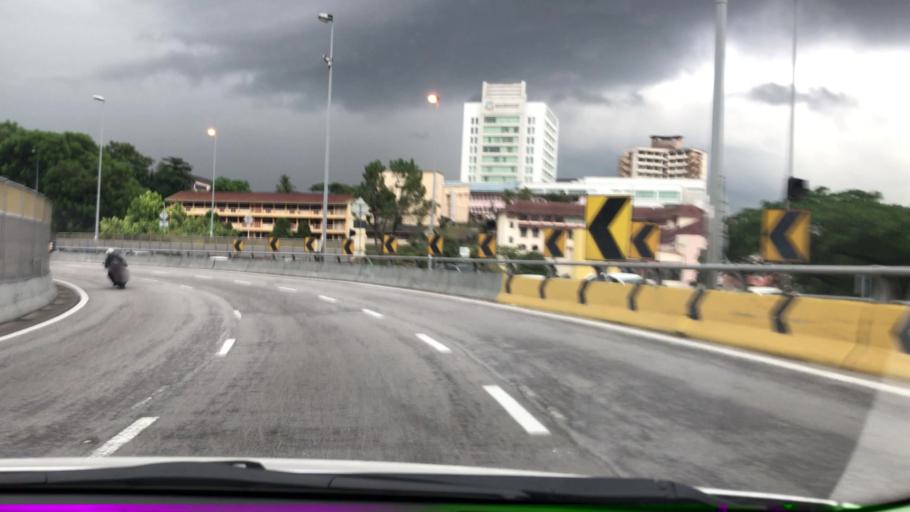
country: MY
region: Kuala Lumpur
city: Kuala Lumpur
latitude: 3.1186
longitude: 101.6635
